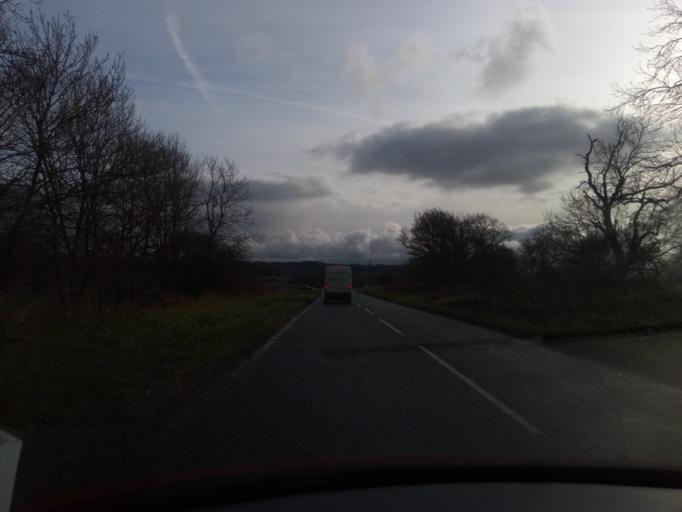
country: GB
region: England
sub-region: Northumberland
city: Wall
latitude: 55.0378
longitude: -2.1373
